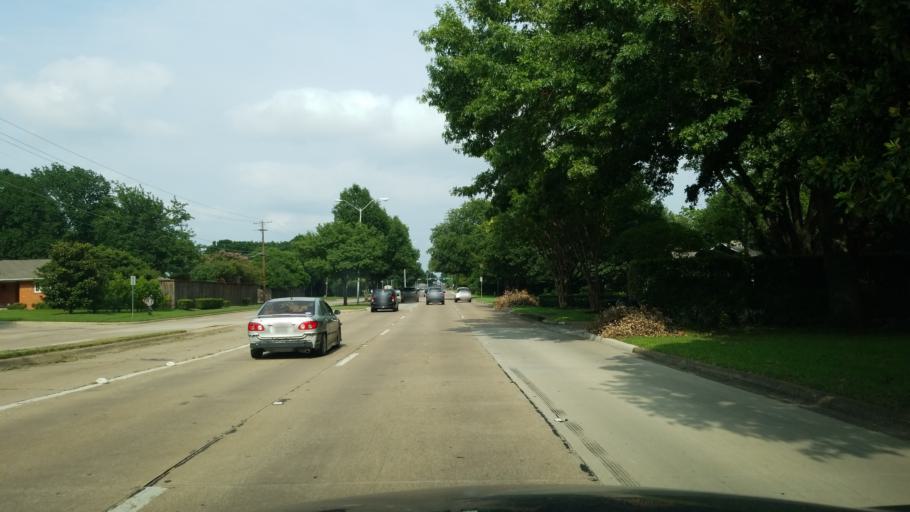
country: US
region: Texas
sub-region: Dallas County
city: University Park
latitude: 32.8949
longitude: -96.8418
